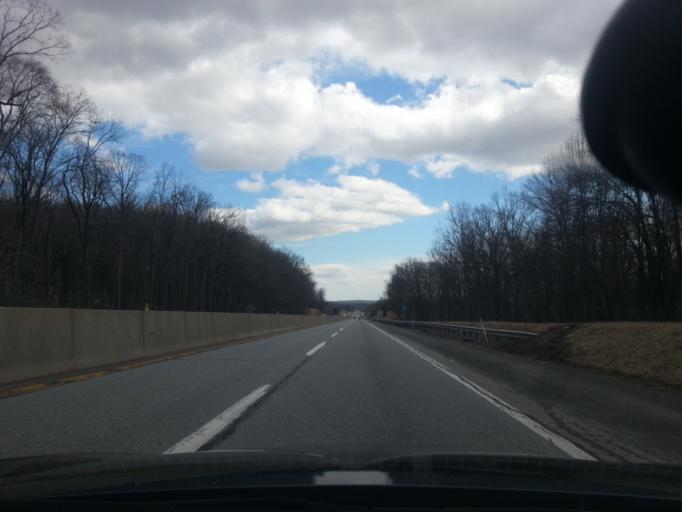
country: US
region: Pennsylvania
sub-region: Bucks County
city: Spinnerstown
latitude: 40.4600
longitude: -75.4443
